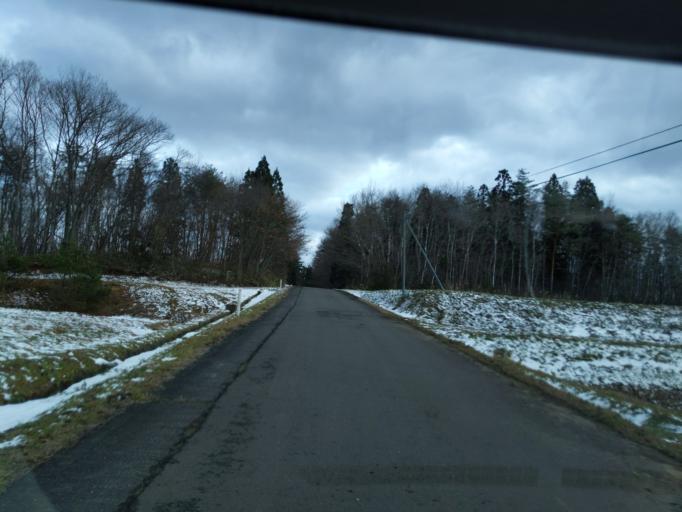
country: JP
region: Iwate
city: Ichinoseki
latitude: 38.9887
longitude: 141.0015
